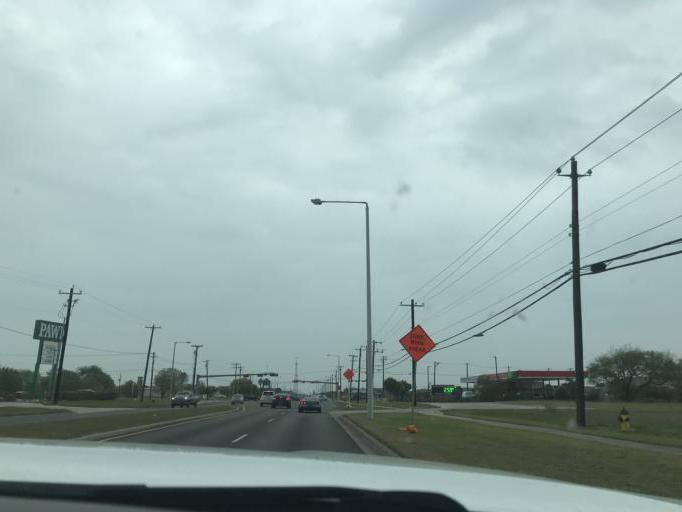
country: US
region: Texas
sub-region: Nueces County
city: Corpus Christi
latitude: 27.6765
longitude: -97.3658
